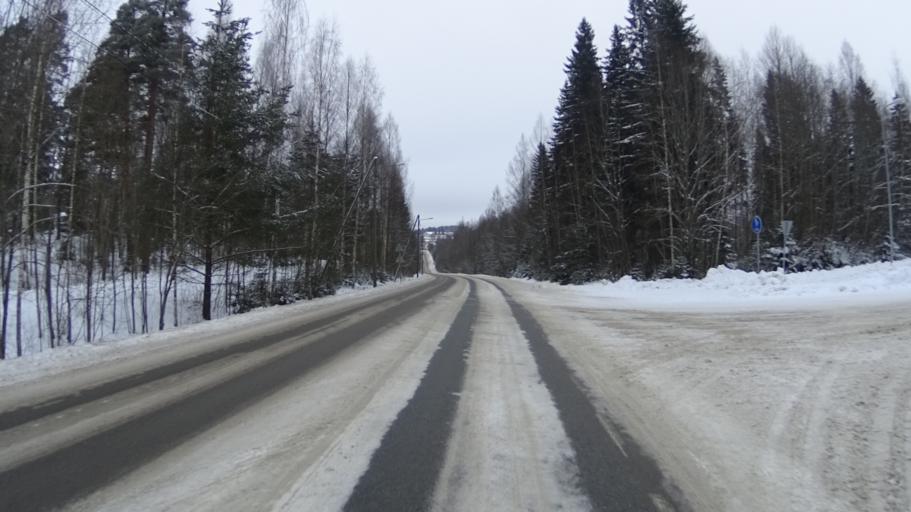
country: FI
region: Uusimaa
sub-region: Helsinki
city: Karkkila
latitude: 60.5264
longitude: 24.2057
